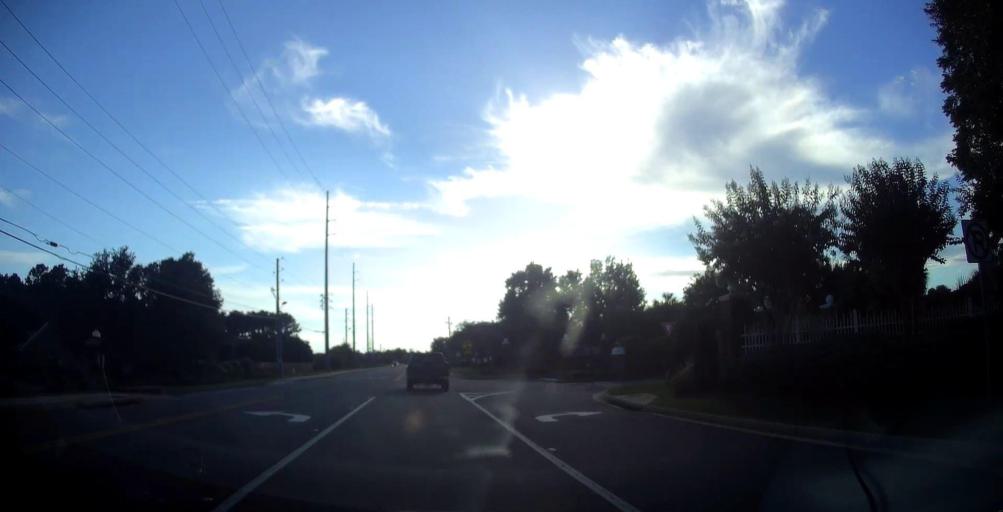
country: US
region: Georgia
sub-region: Houston County
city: Centerville
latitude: 32.6215
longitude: -83.7057
